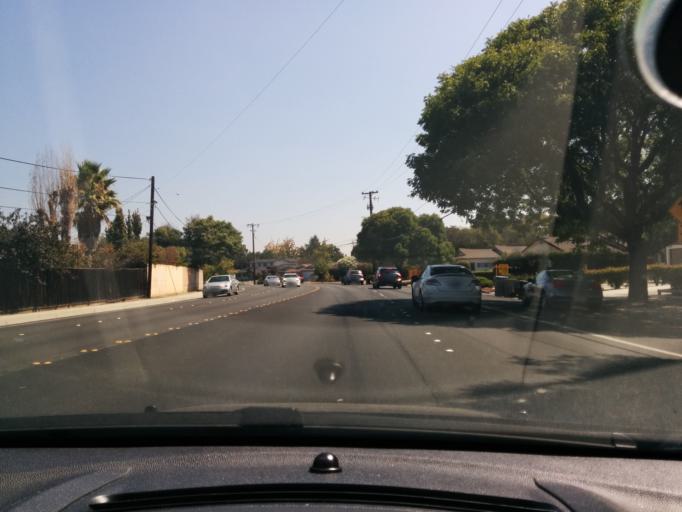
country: US
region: California
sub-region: Santa Clara County
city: Cupertino
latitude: 37.3097
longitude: -122.0226
